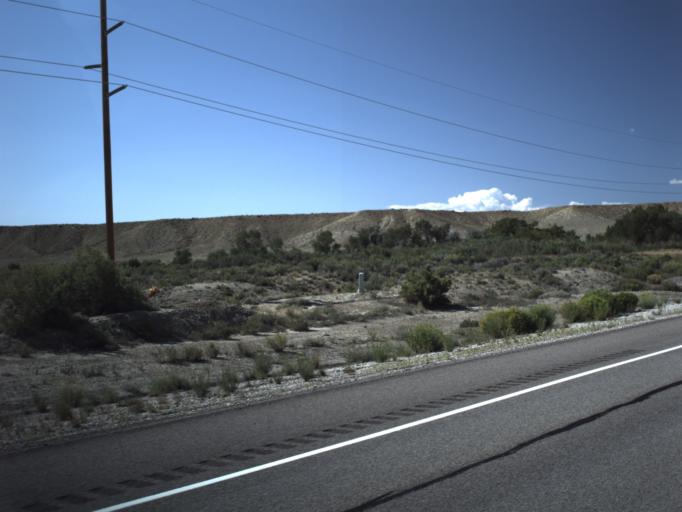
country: US
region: Utah
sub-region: Emery County
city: Ferron
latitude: 38.9377
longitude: -111.2253
